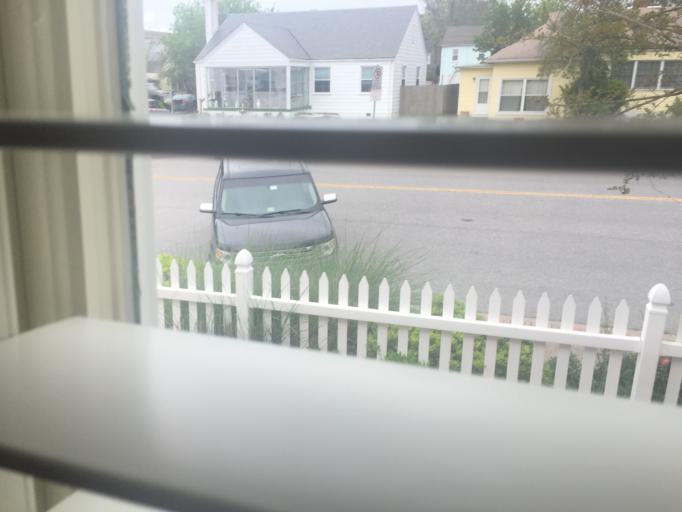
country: US
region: Virginia
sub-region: City of Virginia Beach
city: Virginia Beach
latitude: 36.8516
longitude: -75.9803
